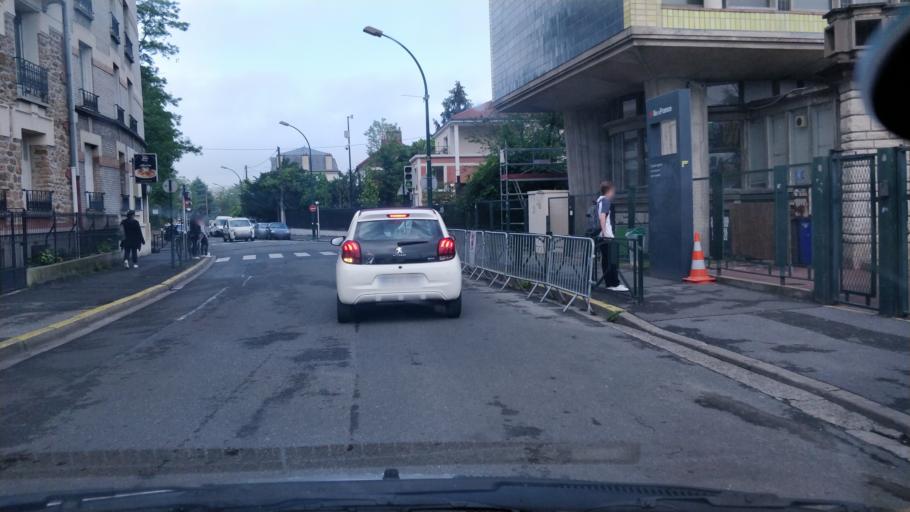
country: FR
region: Ile-de-France
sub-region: Departement de Seine-Saint-Denis
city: Le Raincy
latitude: 48.8988
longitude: 2.5108
